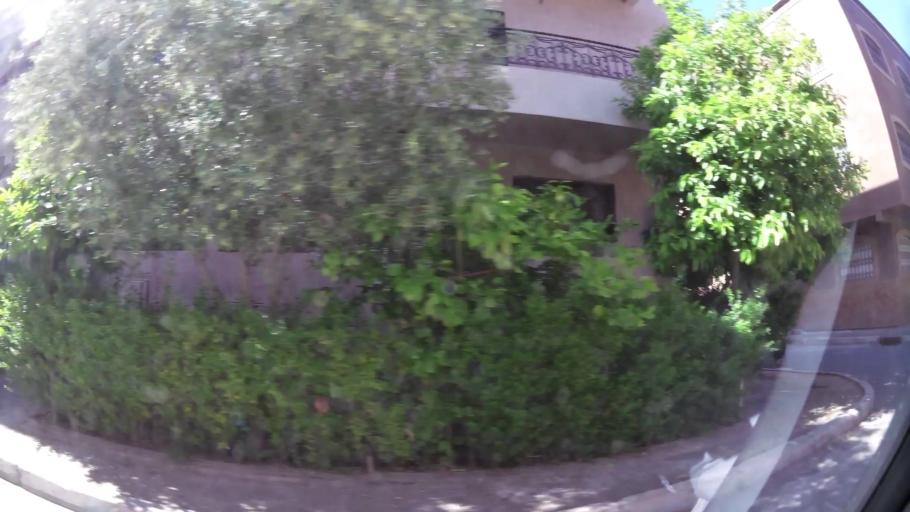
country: MA
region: Marrakech-Tensift-Al Haouz
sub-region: Marrakech
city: Marrakesh
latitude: 31.6669
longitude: -8.0248
